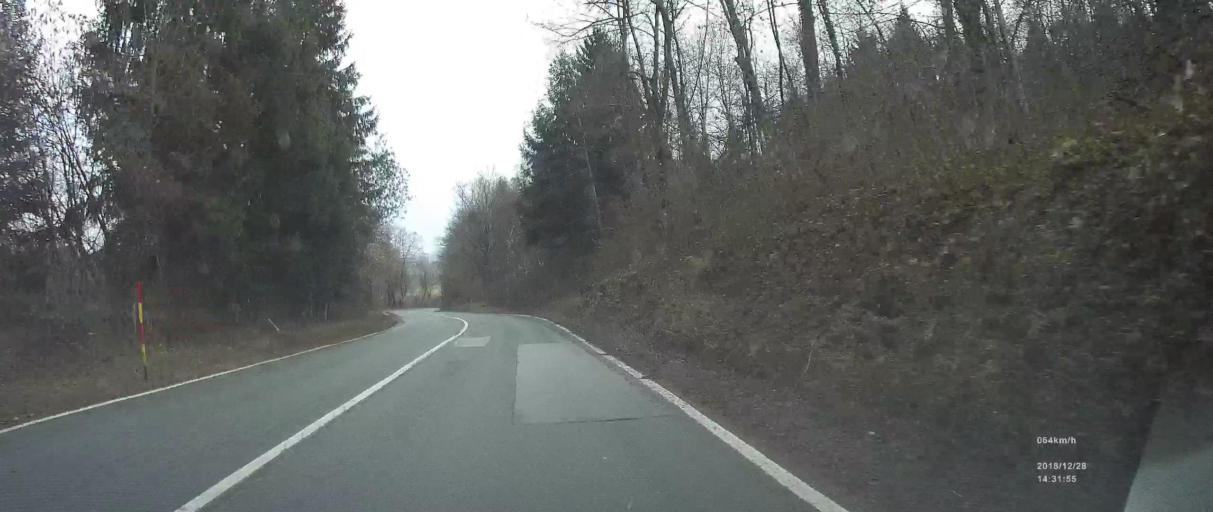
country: HR
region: Primorsko-Goranska
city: Vrbovsko
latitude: 45.4147
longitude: 15.1490
